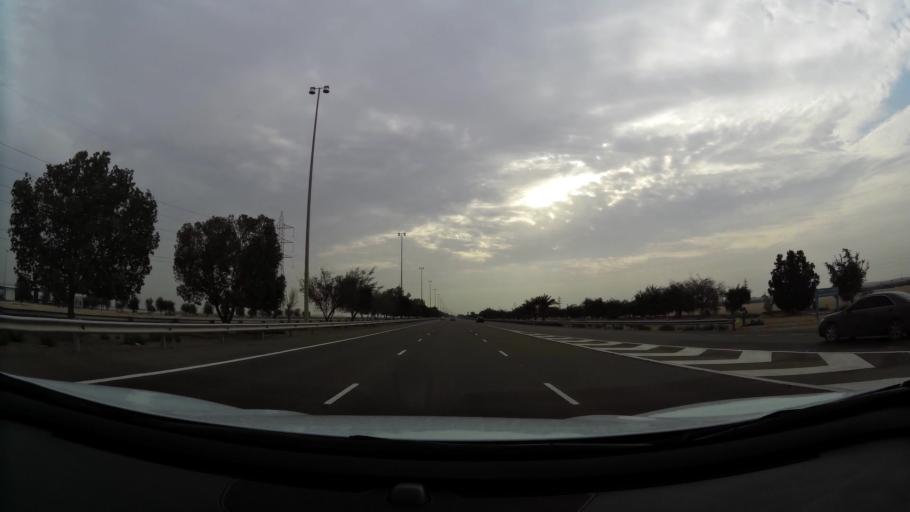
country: AE
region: Abu Dhabi
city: Abu Dhabi
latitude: 24.2183
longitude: 54.8548
